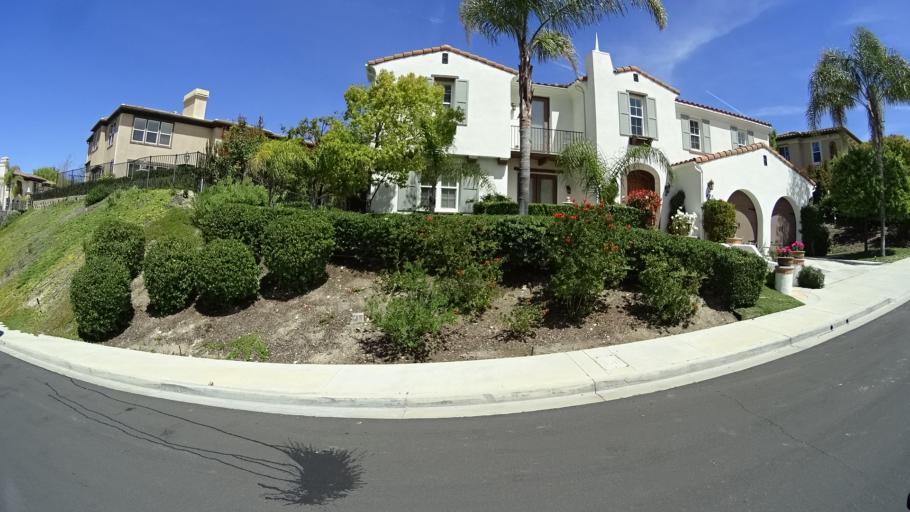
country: US
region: California
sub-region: Ventura County
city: Thousand Oaks
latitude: 34.1808
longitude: -118.8382
